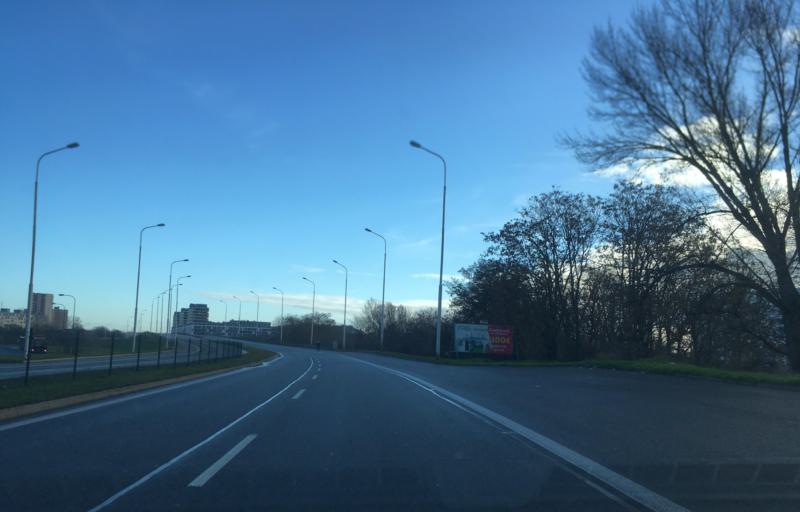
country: AT
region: Burgenland
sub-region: Politischer Bezirk Neusiedl am See
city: Kittsee
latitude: 48.0946
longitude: 17.1045
